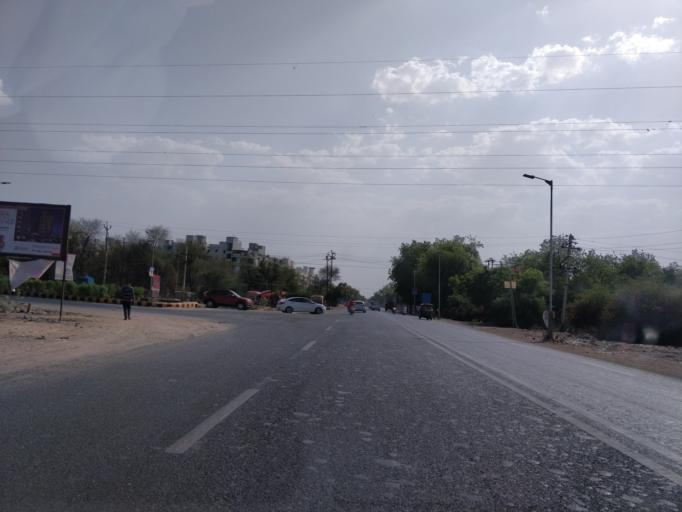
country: IN
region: Gujarat
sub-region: Ahmadabad
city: Naroda
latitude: 23.0813
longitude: 72.6722
